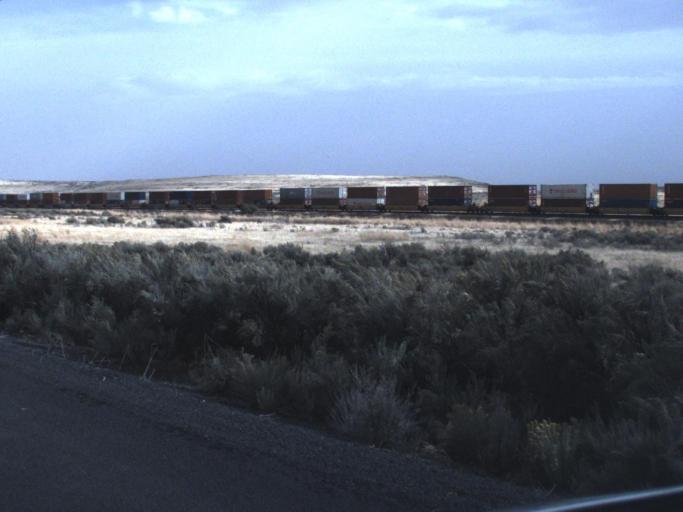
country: US
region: Washington
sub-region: Adams County
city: Ritzville
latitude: 47.3477
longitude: -118.5852
